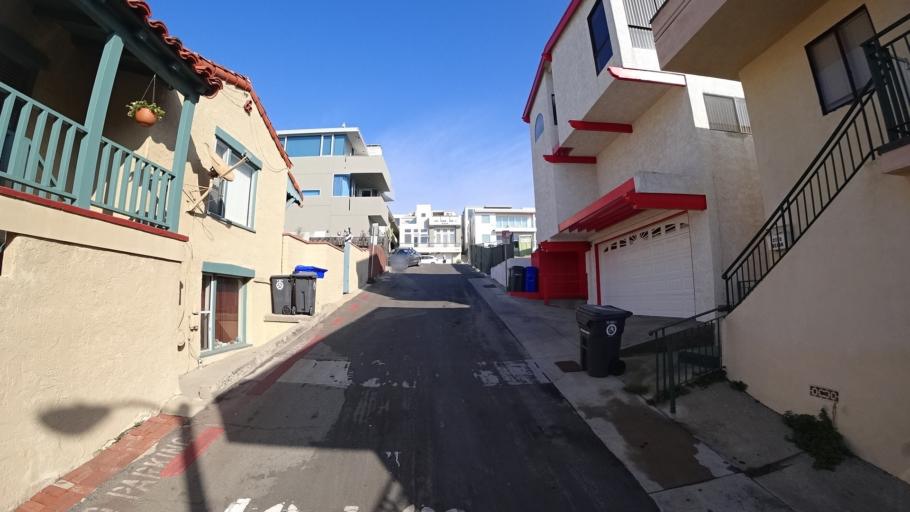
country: US
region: California
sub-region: Los Angeles County
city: Manhattan Beach
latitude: 33.8946
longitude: -118.4166
